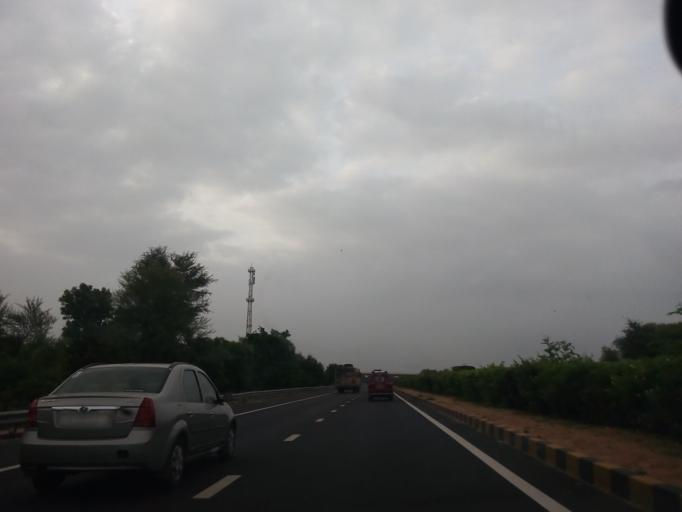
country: IN
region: Gujarat
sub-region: Kheda
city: Mahemdavad
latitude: 22.8964
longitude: 72.7800
